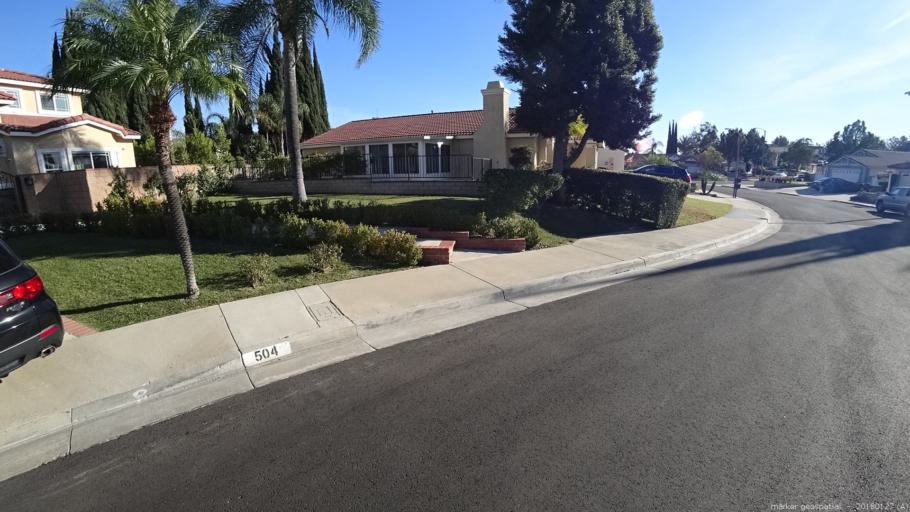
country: US
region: California
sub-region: Los Angeles County
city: Diamond Bar
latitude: 34.0196
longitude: -117.7920
